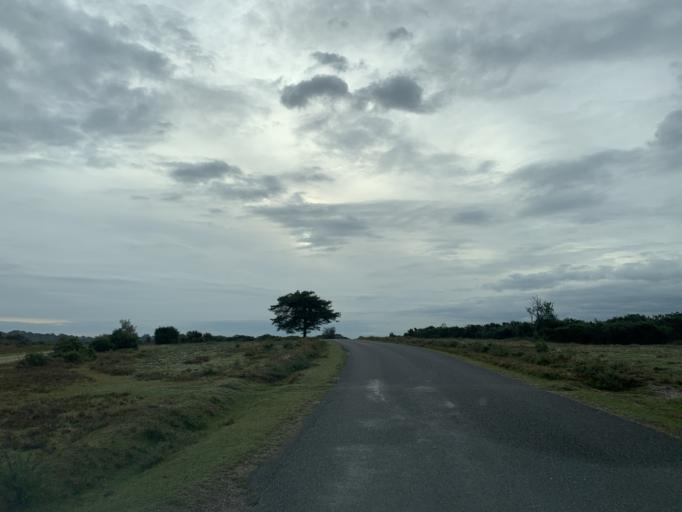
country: GB
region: England
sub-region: Hampshire
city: Sway
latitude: 50.8231
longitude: -1.6150
